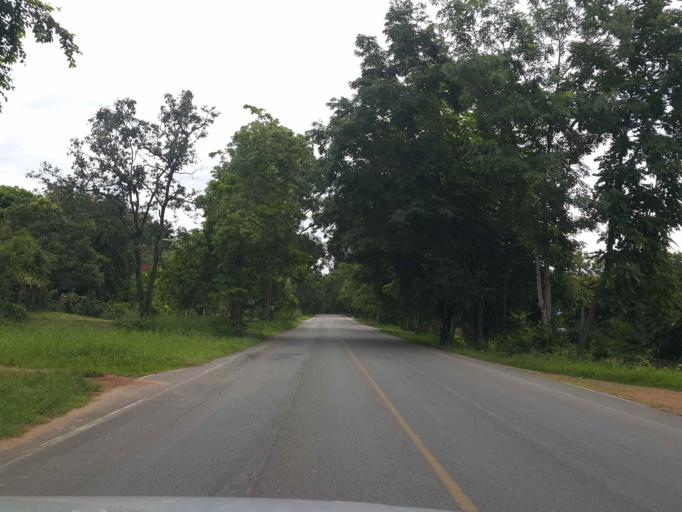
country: TH
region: Lampang
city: Thoen
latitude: 17.5500
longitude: 99.3383
